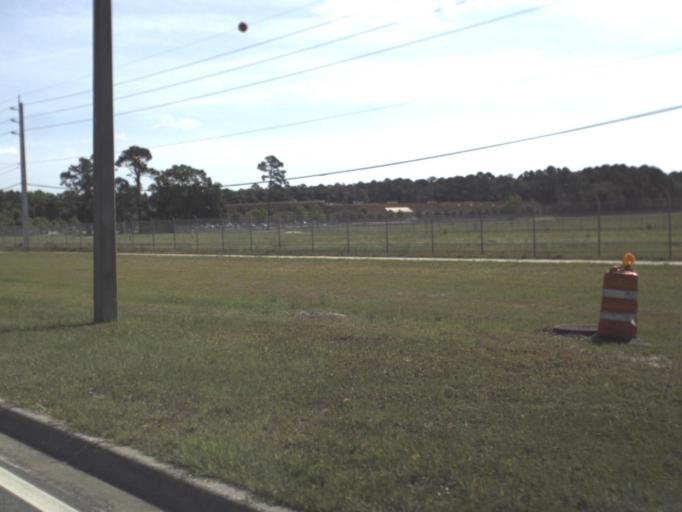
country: US
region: Florida
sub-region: Clay County
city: Orange Park
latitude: 30.2325
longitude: -81.6985
